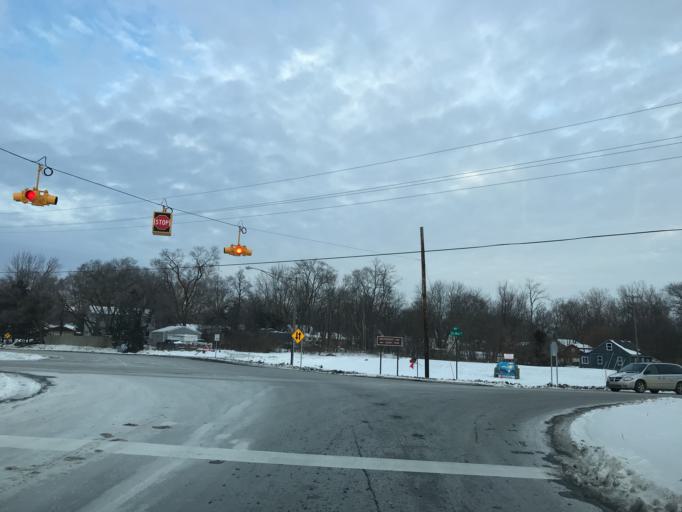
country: US
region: Michigan
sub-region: Livingston County
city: Whitmore Lake
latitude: 42.3938
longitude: -83.7622
